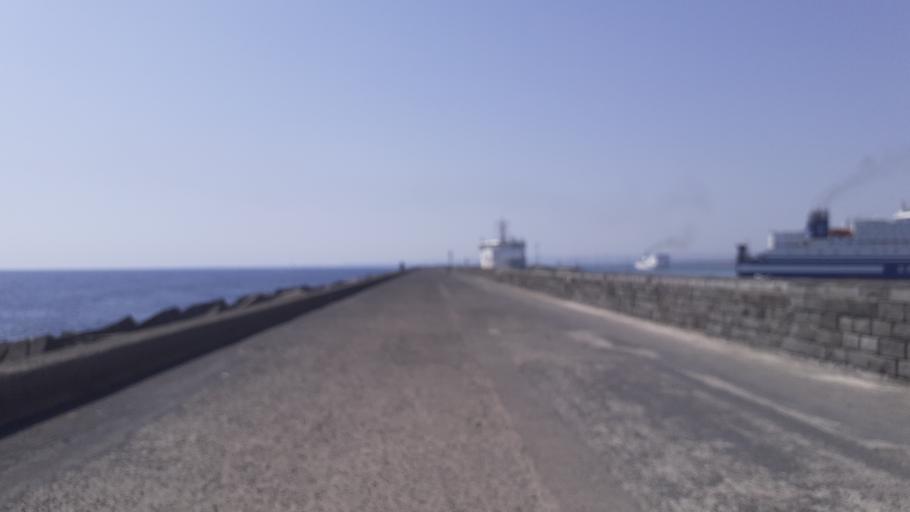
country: IT
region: Sicily
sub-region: Catania
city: Catania
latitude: 37.4969
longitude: 15.0994
